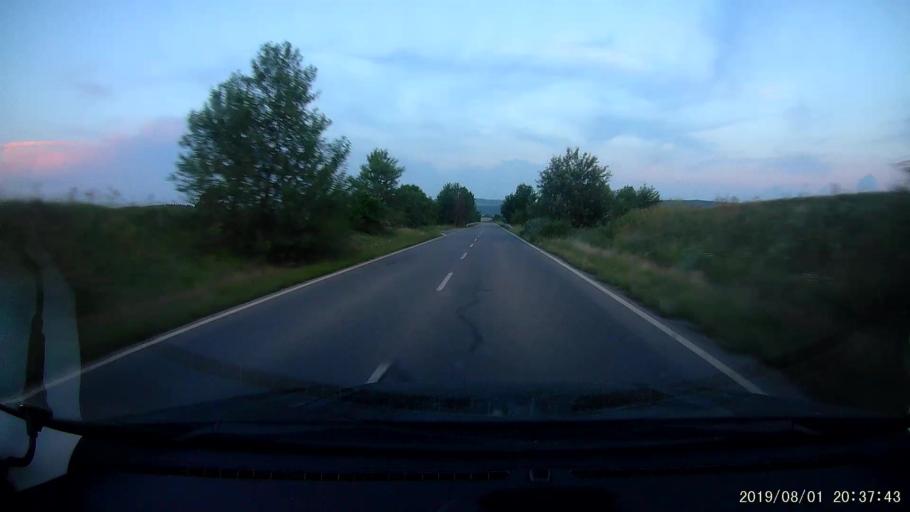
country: BG
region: Yambol
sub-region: Obshtina Elkhovo
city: Elkhovo
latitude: 42.0419
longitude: 26.5954
